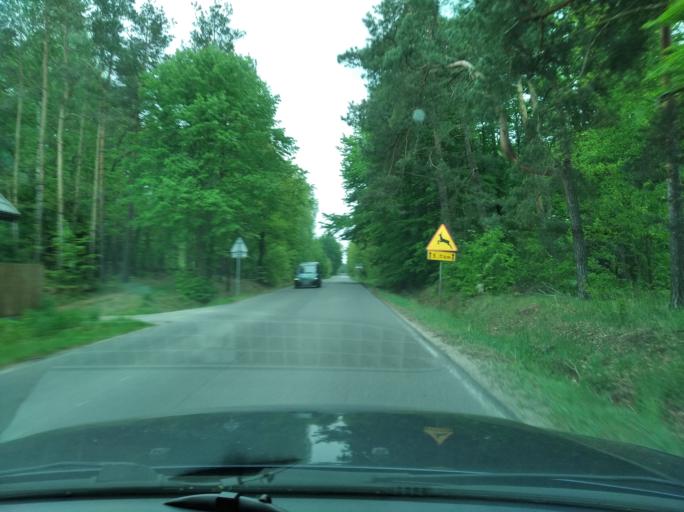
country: PL
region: Subcarpathian Voivodeship
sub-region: Powiat kolbuszowski
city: Kolbuszowa
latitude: 50.1767
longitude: 21.7591
